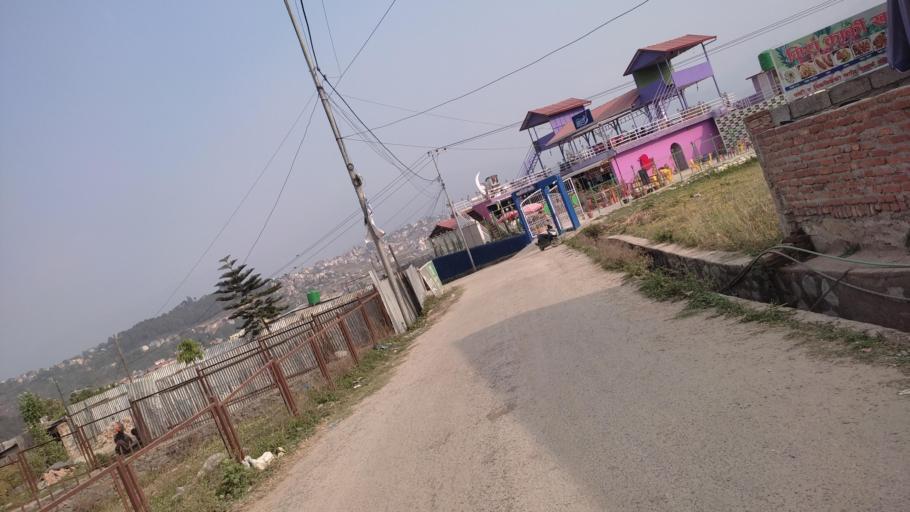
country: NP
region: Central Region
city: Kirtipur
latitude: 27.6609
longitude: 85.2816
